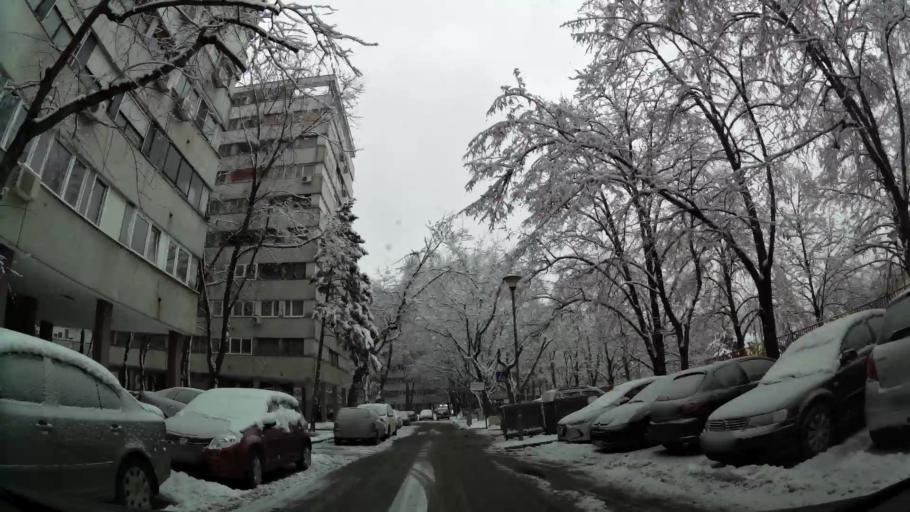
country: RS
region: Central Serbia
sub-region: Belgrade
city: Novi Beograd
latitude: 44.8179
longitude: 20.4044
